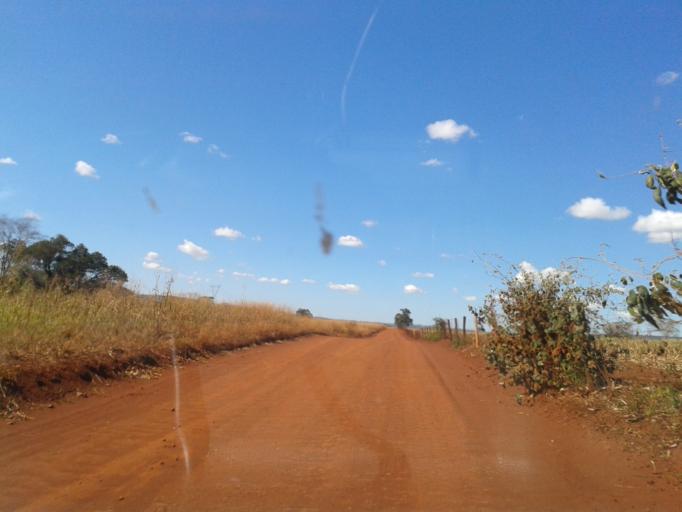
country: BR
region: Minas Gerais
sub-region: Centralina
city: Centralina
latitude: -18.5789
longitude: -49.1327
